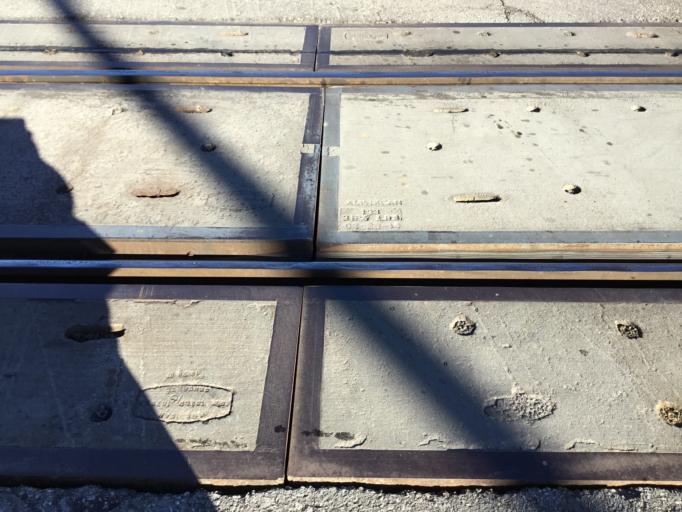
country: US
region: Kansas
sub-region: Douglas County
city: Lawrence
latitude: 38.9784
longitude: -95.2332
